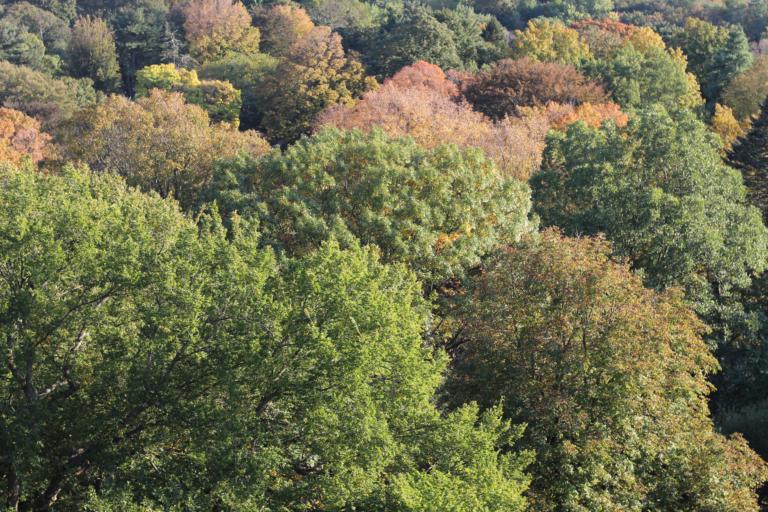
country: US
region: Massachusetts
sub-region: Middlesex County
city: Watertown
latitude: 42.3707
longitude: -71.1452
